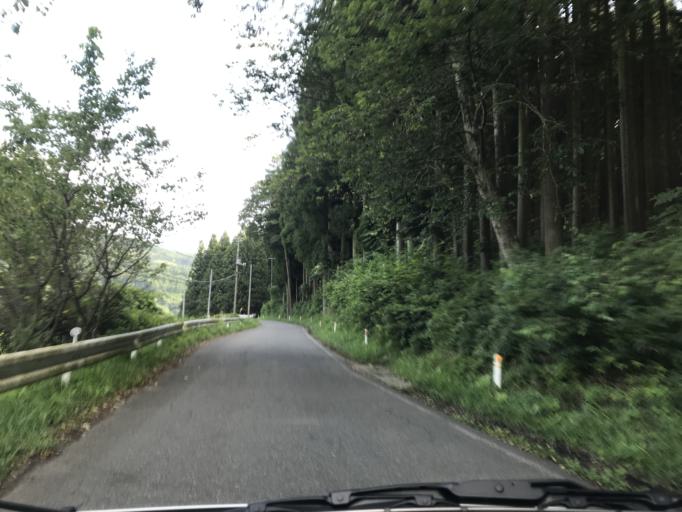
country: JP
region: Iwate
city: Ofunato
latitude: 38.9606
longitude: 141.4713
